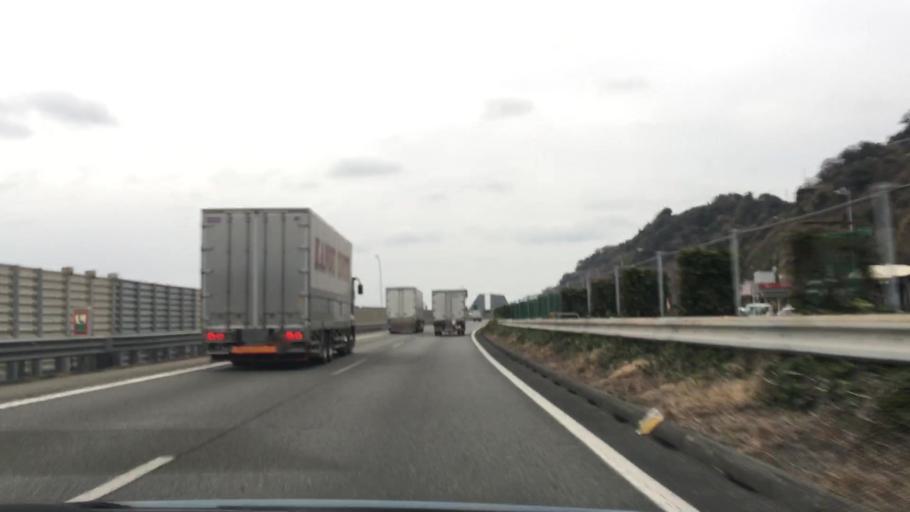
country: JP
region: Shizuoka
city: Fujinomiya
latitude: 35.0775
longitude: 138.5466
